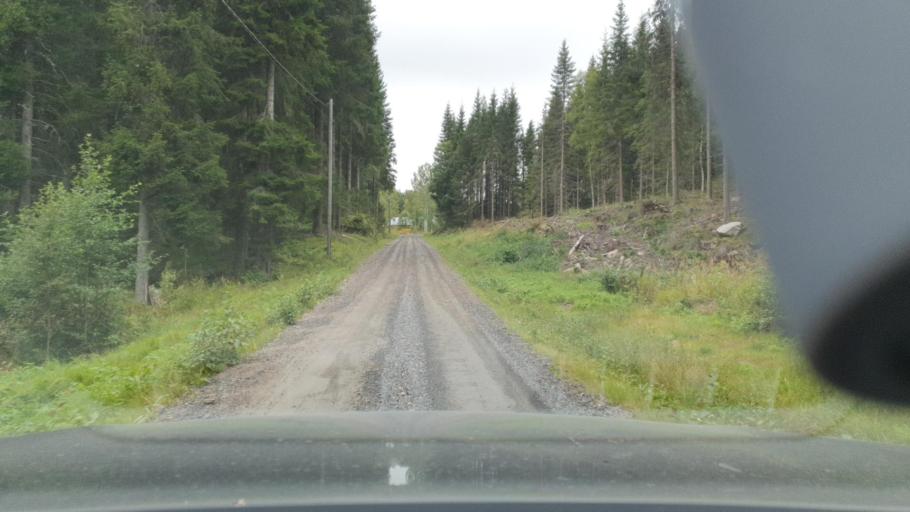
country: SE
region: Vaermland
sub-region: Torsby Kommun
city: Torsby
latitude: 60.3425
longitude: 12.6171
